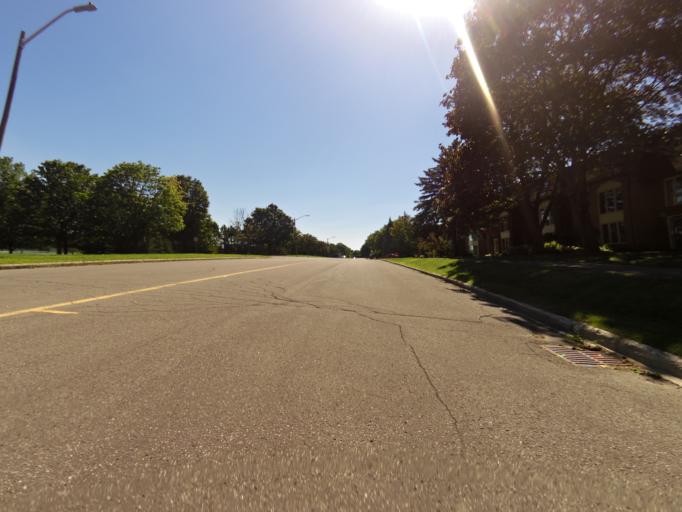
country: CA
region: Ontario
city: Ottawa
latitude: 45.3546
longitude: -75.6667
